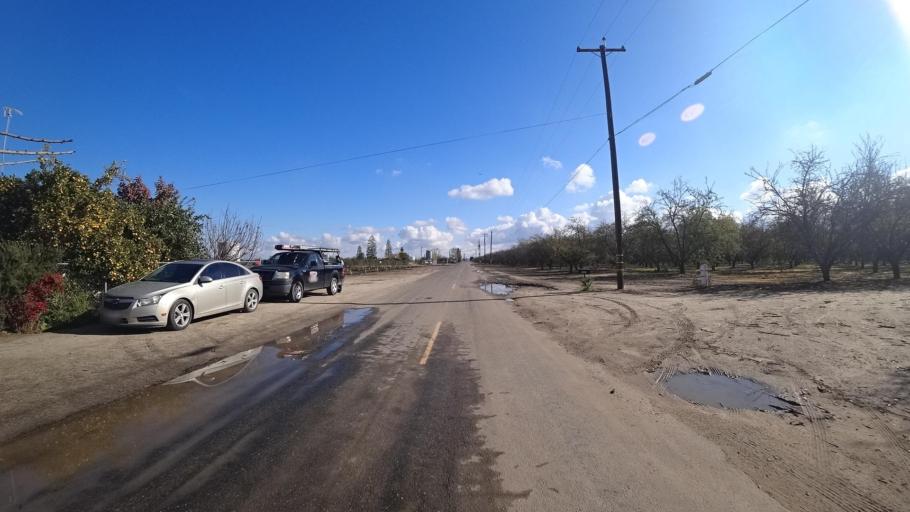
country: US
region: California
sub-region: Kern County
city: McFarland
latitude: 35.6598
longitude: -119.2502
